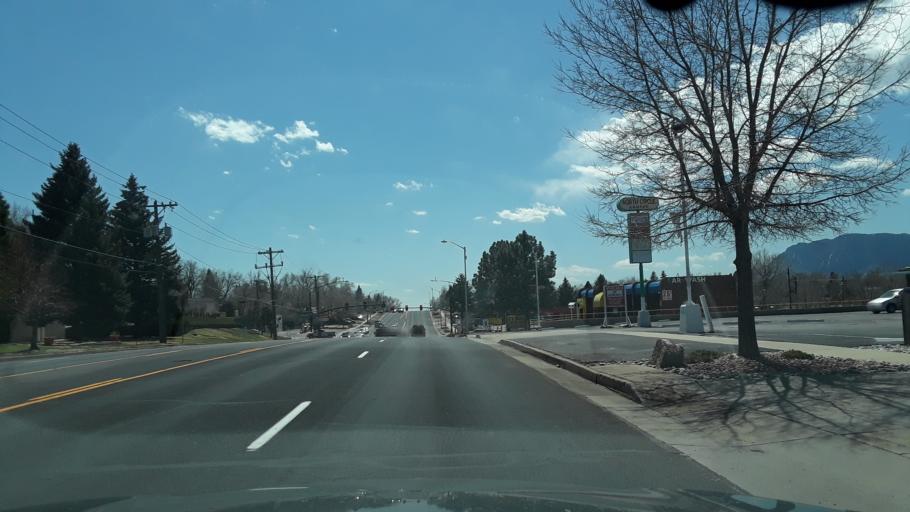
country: US
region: Colorado
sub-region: El Paso County
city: Colorado Springs
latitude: 38.8557
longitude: -104.7759
